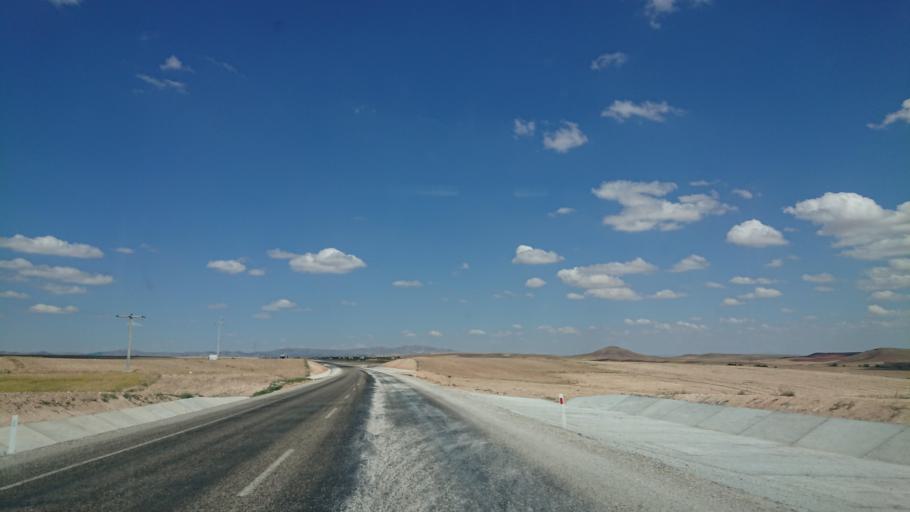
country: TR
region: Kirsehir
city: Kirsehir
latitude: 39.1219
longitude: 34.0130
